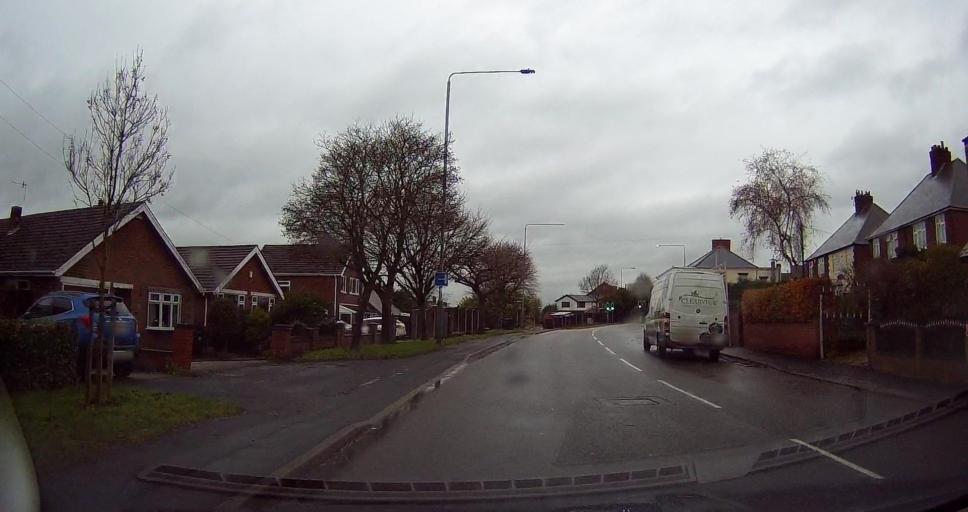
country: GB
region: England
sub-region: Nottinghamshire
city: Kimberley
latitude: 52.9996
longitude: -1.2698
